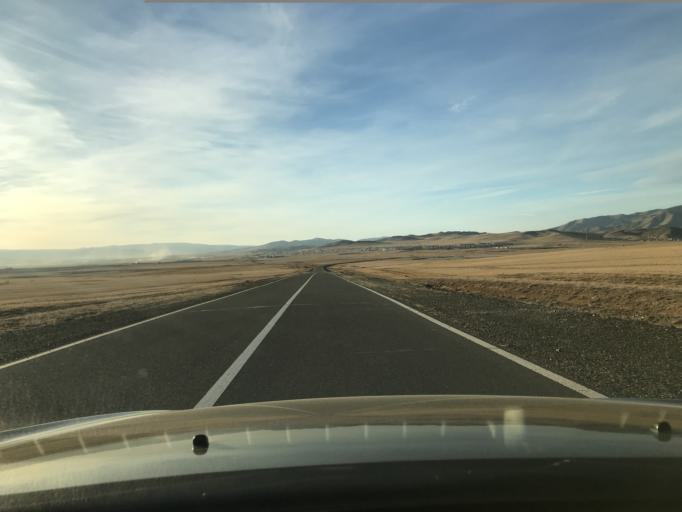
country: MN
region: Central Aimak
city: Arhust
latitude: 47.7644
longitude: 107.4308
